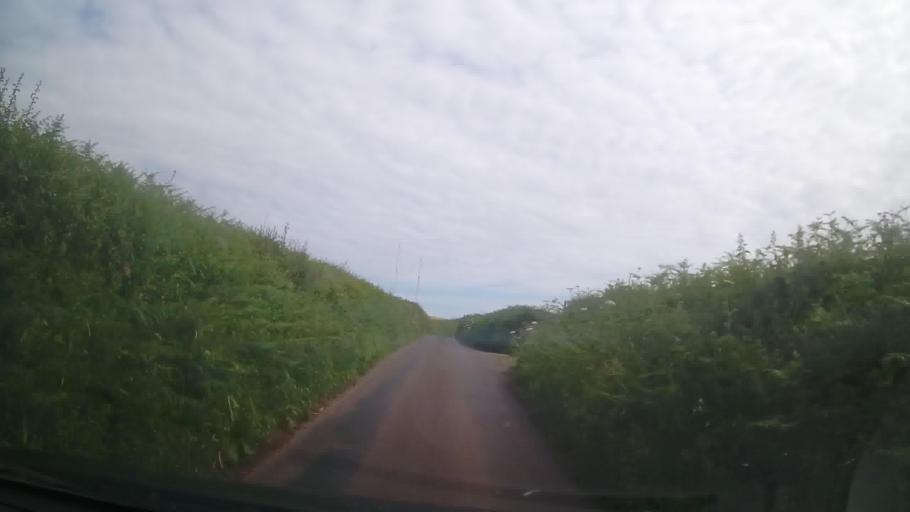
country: GB
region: England
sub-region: Devon
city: Salcombe
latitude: 50.2344
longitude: -3.6721
